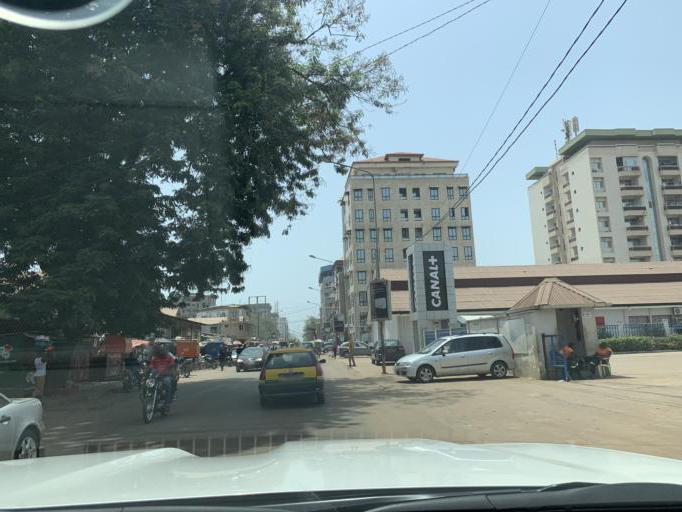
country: GN
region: Conakry
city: Camayenne
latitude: 9.5129
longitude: -13.7062
